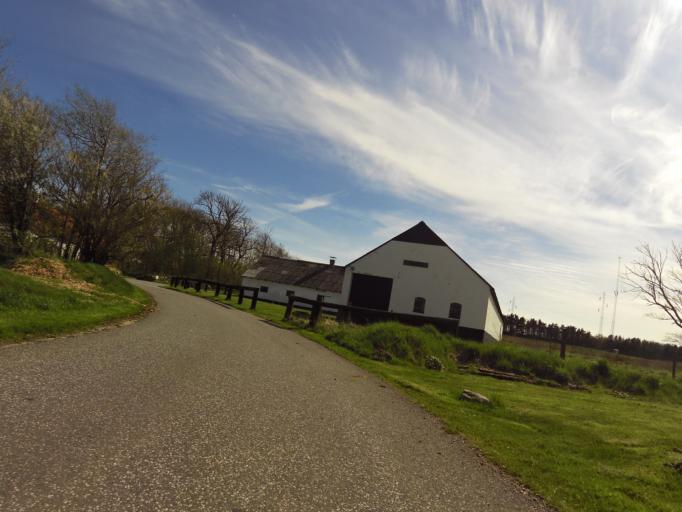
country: DK
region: Central Jutland
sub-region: Skive Kommune
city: Skive
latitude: 56.5653
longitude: 8.9853
